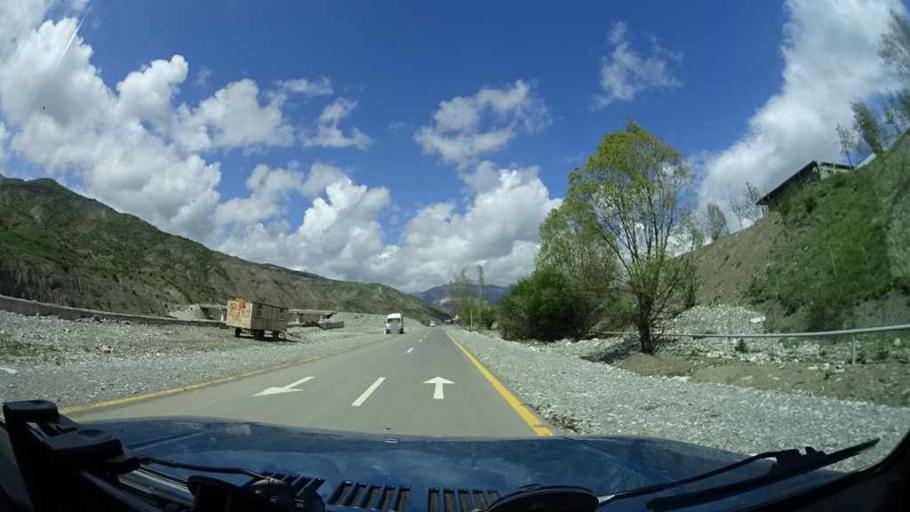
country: AZ
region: Ismayilli
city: Basqal
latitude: 40.8494
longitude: 48.3840
